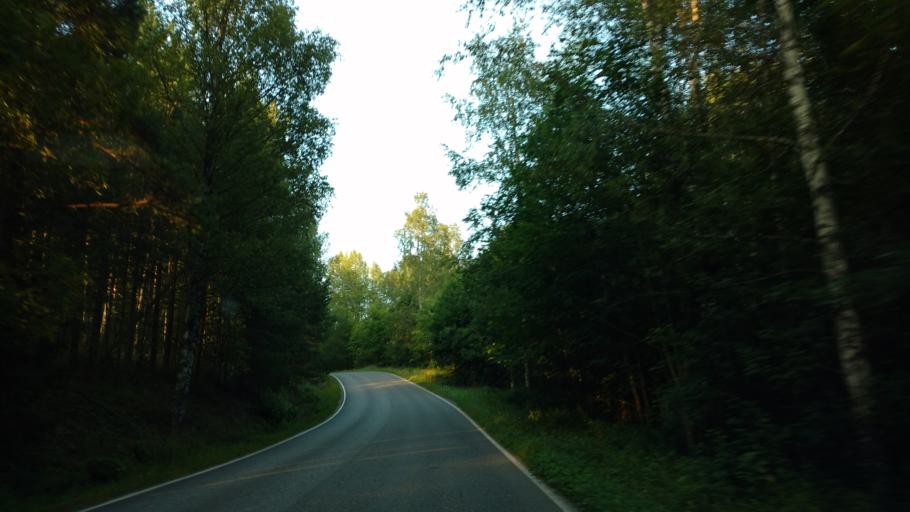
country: FI
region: Varsinais-Suomi
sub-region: Salo
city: Saerkisalo
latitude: 60.2189
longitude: 22.9119
